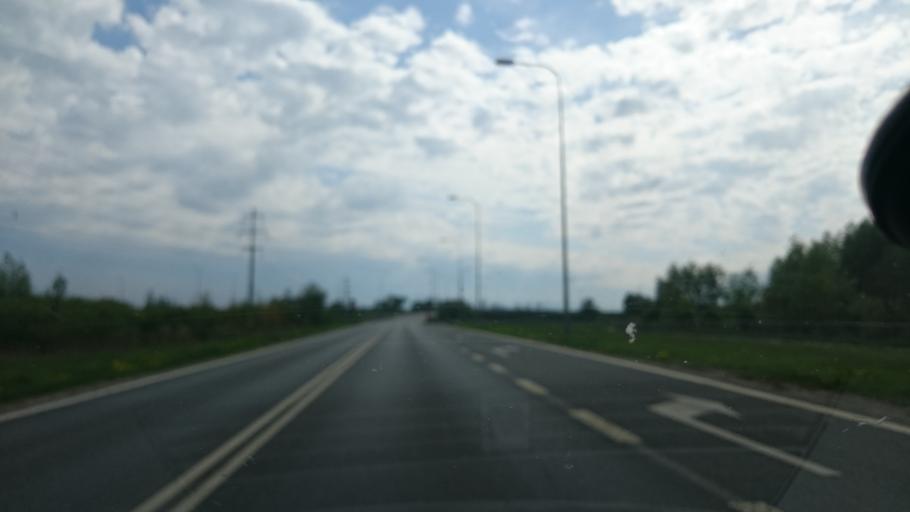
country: PL
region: Kujawsko-Pomorskie
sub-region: Grudziadz
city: Grudziadz
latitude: 53.4860
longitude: 18.7923
